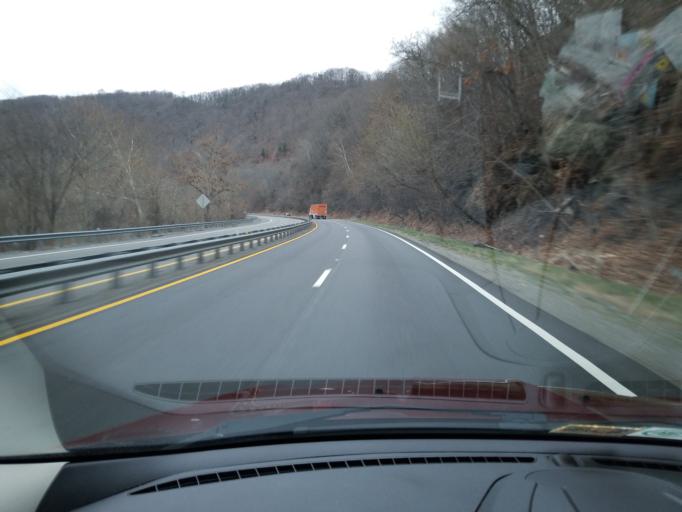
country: US
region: Virginia
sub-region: Giles County
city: Narrows
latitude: 37.3876
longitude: -80.8291
